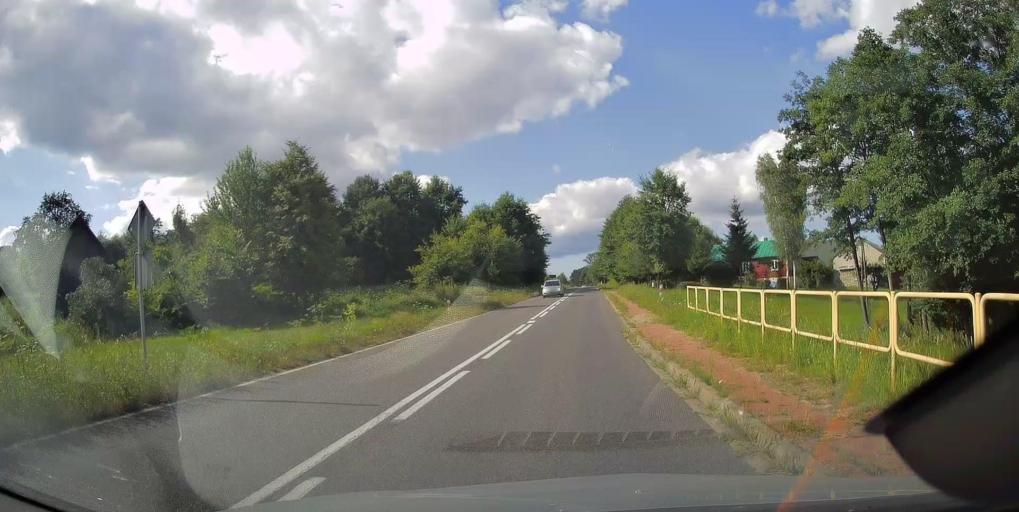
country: PL
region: Swietokrzyskie
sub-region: Powiat kielecki
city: Nowa Slupia
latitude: 50.8845
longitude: 21.0468
